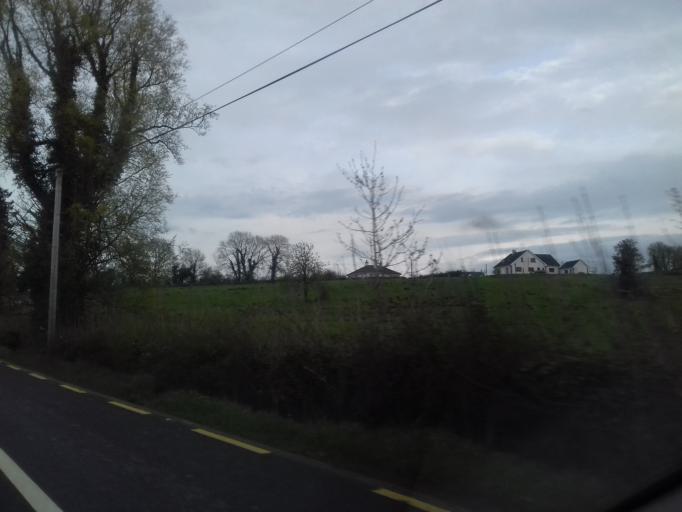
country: IE
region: Ulster
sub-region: An Cabhan
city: Belturbet
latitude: 54.0889
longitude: -7.5013
